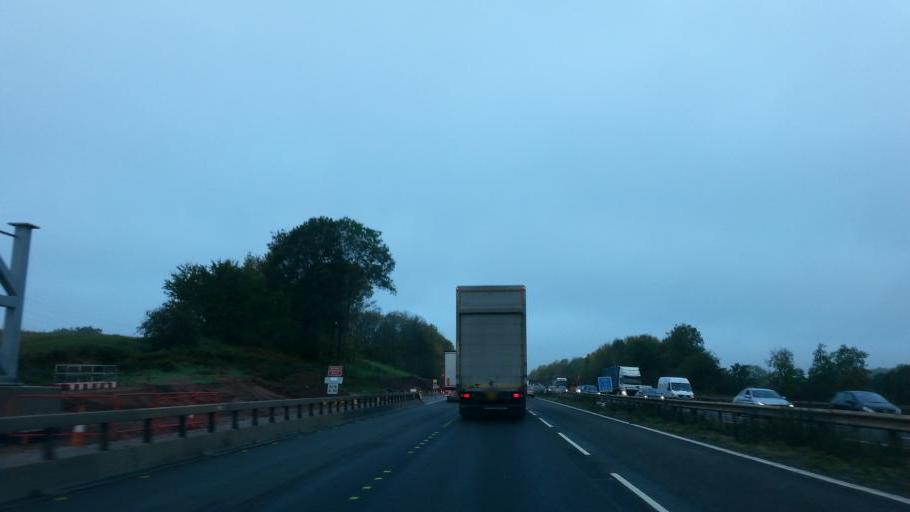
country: GB
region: England
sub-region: Coventry
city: Keresley
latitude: 52.4682
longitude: -1.5202
